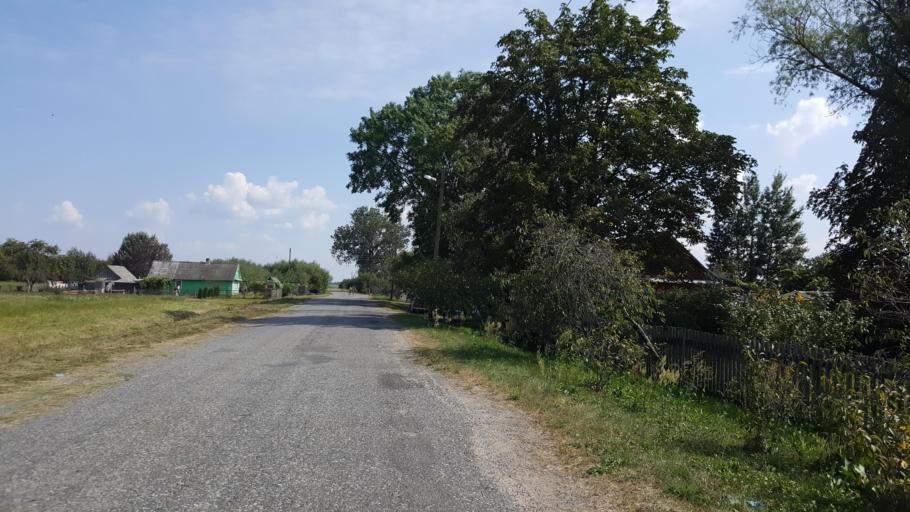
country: BY
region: Brest
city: Kamyanyuki
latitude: 52.4921
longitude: 23.5827
